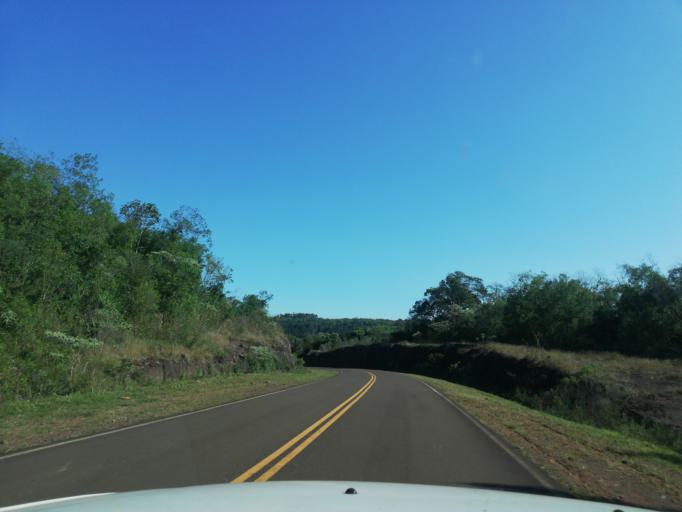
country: AR
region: Misiones
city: Arroyo del Medio
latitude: -27.6539
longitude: -55.4024
